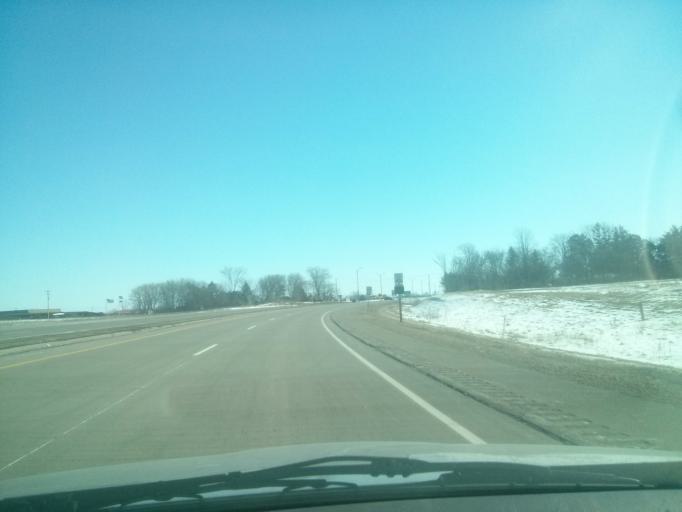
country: US
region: Wisconsin
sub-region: Saint Croix County
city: New Richmond
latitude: 45.1324
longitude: -92.5528
